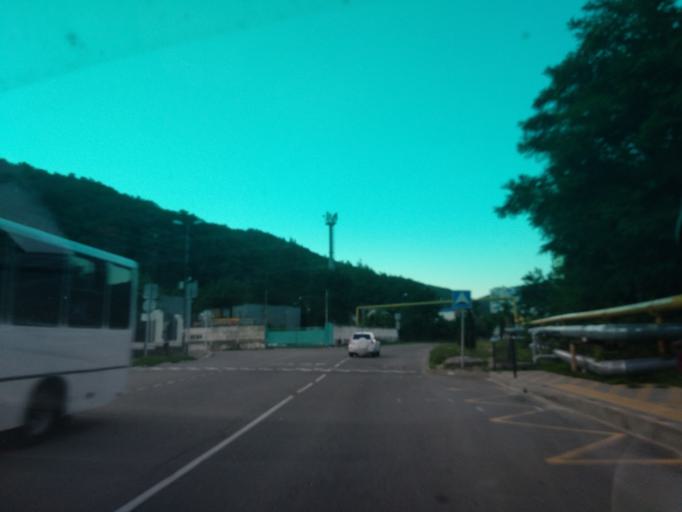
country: RU
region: Krasnodarskiy
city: Tuapse
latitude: 44.1206
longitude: 39.0702
